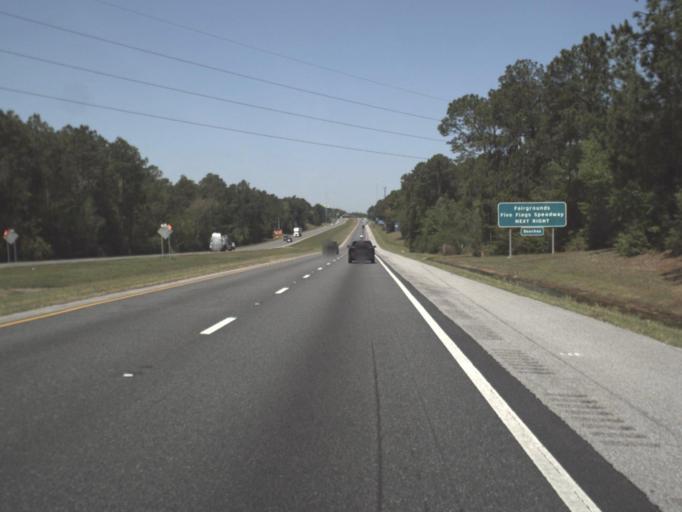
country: US
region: Florida
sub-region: Escambia County
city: Ensley
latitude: 30.5142
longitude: -87.2996
